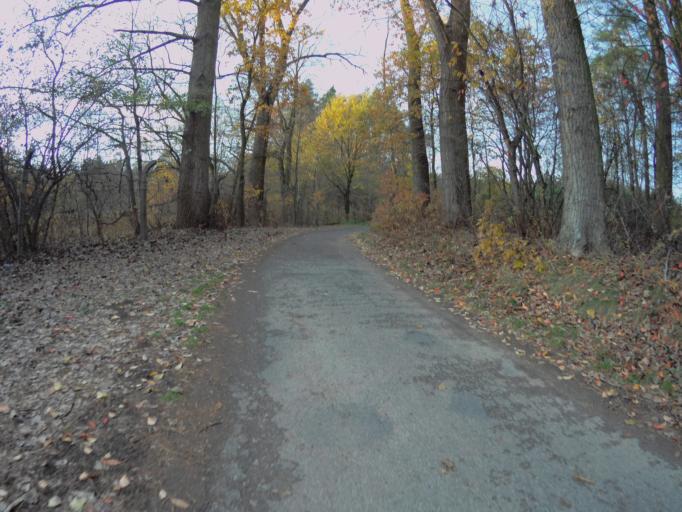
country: PL
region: Subcarpathian Voivodeship
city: Nowa Sarzyna
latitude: 50.3154
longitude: 22.3341
